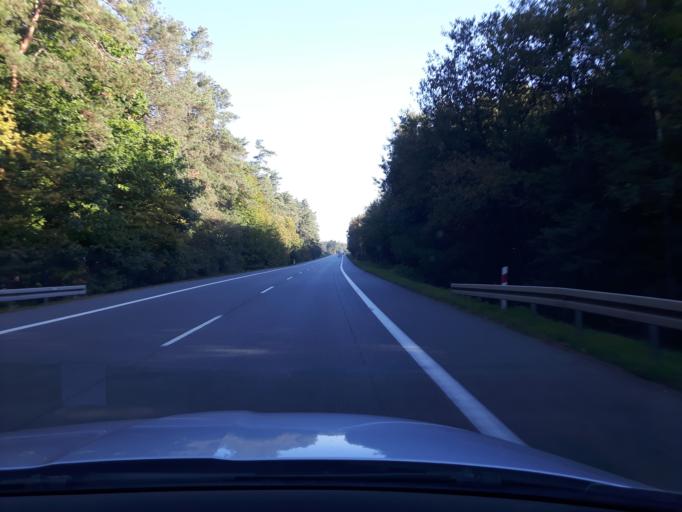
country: PL
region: Masovian Voivodeship
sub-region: Powiat mlawski
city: Mlawa
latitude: 53.1361
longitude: 20.3964
